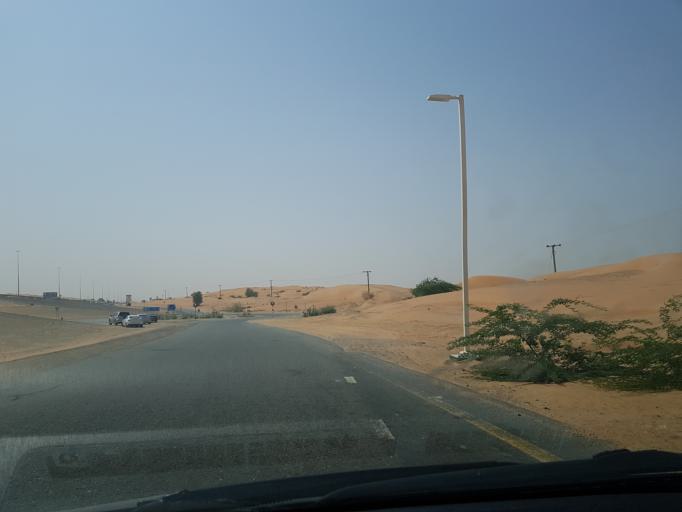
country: AE
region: Ra's al Khaymah
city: Ras al-Khaimah
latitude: 25.6204
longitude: 55.8012
